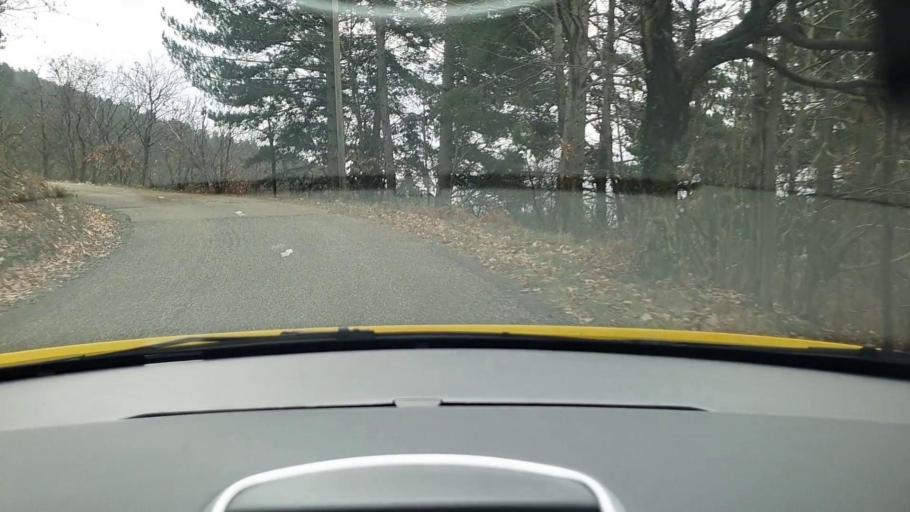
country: FR
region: Languedoc-Roussillon
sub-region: Departement du Gard
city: Besseges
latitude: 44.3729
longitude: 4.0365
